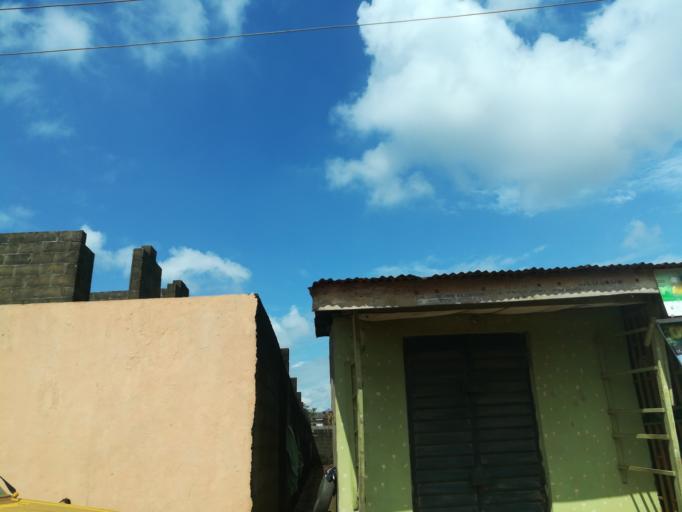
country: NG
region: Lagos
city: Ikorodu
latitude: 6.5945
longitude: 3.5207
